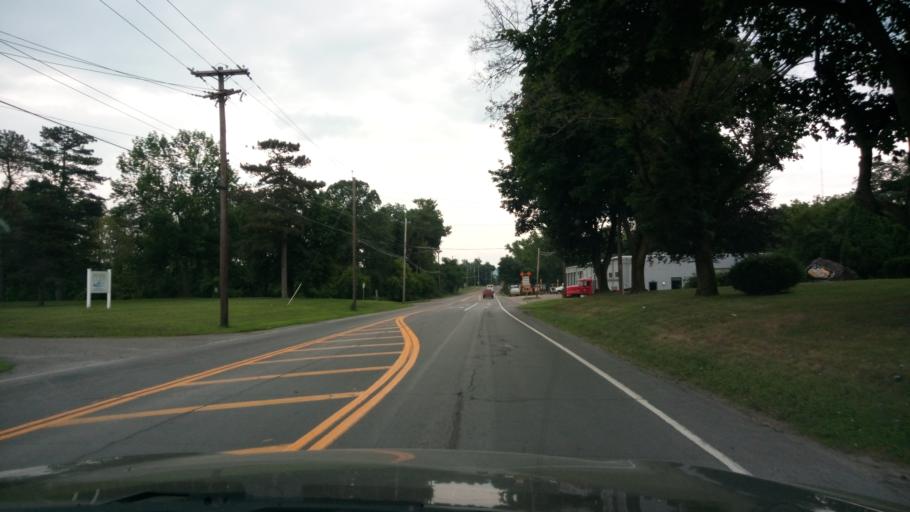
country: US
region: New York
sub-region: Chemung County
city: Elmira Heights
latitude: 42.1208
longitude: -76.8092
